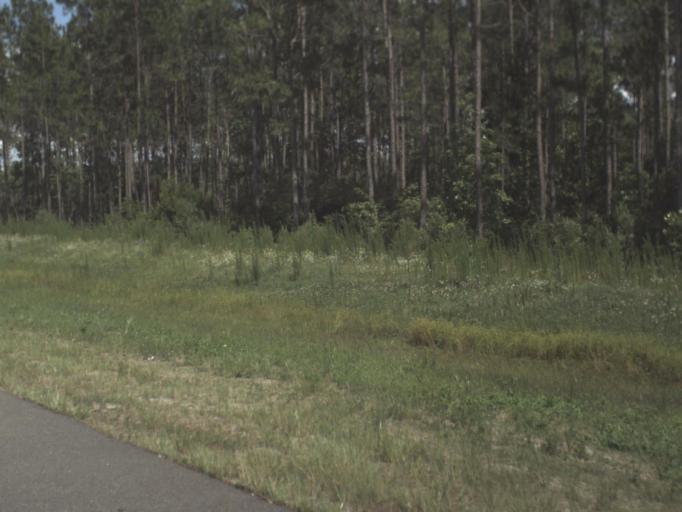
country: US
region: Florida
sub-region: Alachua County
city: Waldo
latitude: 29.7139
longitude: -82.1521
